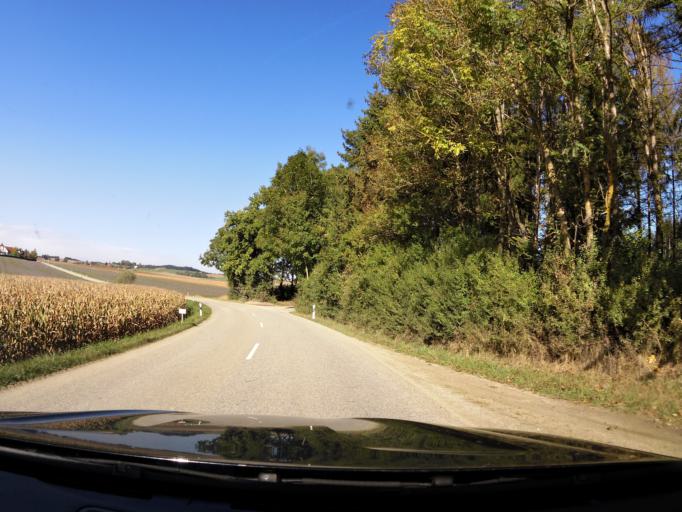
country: DE
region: Bavaria
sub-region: Lower Bavaria
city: Tiefenbach
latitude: 48.4879
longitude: 12.1059
